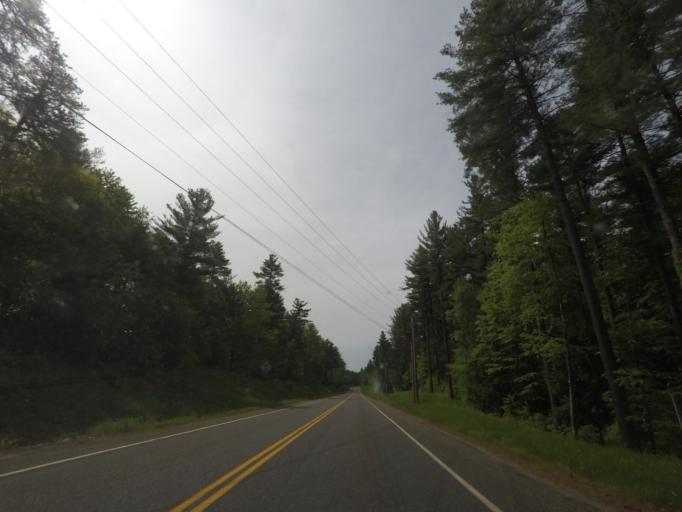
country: US
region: New York
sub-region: Saratoga County
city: Country Knolls
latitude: 42.9768
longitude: -73.7447
